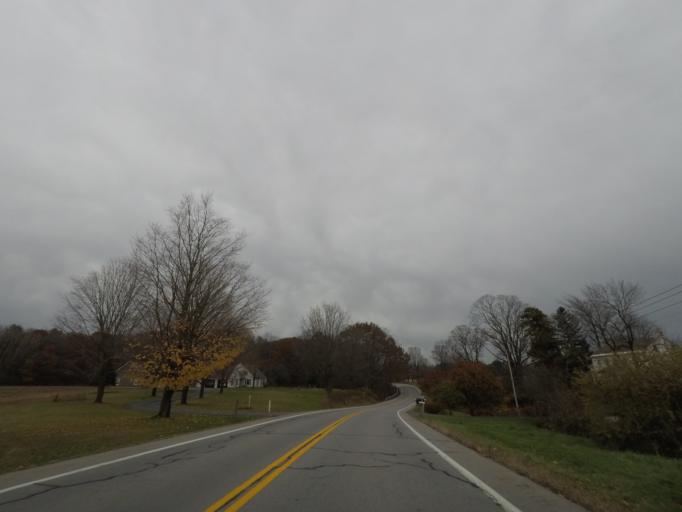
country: US
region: New York
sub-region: Schenectady County
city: Niskayuna
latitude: 42.8208
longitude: -73.8258
